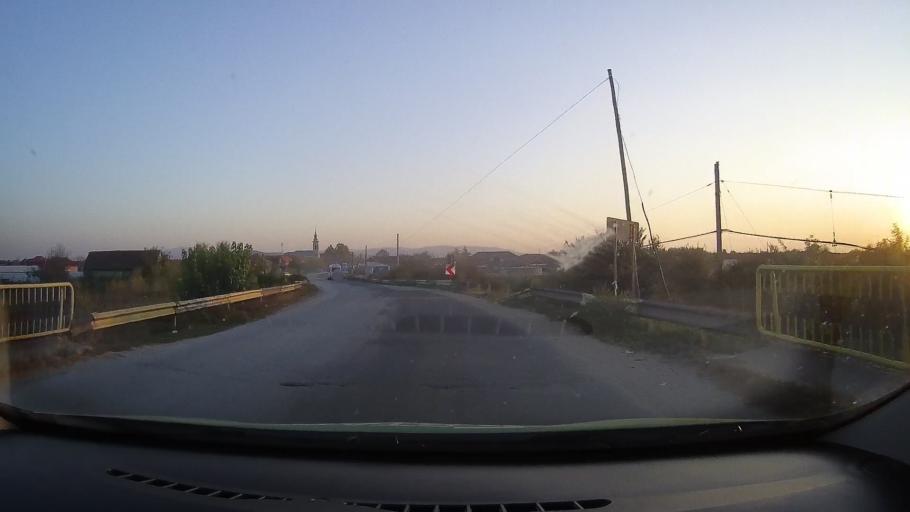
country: RO
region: Arad
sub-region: Comuna Seleus
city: Seleus
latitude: 46.3868
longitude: 21.7072
